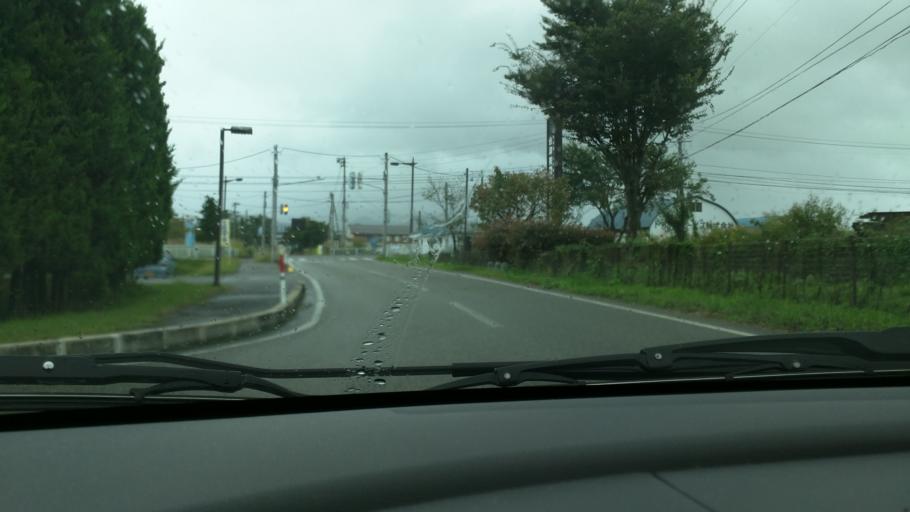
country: JP
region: Fukushima
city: Kitakata
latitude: 37.4711
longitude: 139.8585
